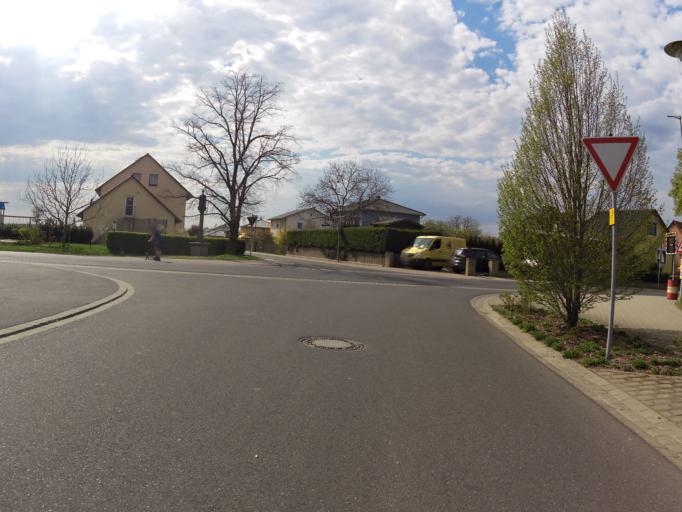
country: DE
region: Bavaria
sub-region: Regierungsbezirk Unterfranken
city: Oberpleichfeld
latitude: 49.8755
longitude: 10.0857
